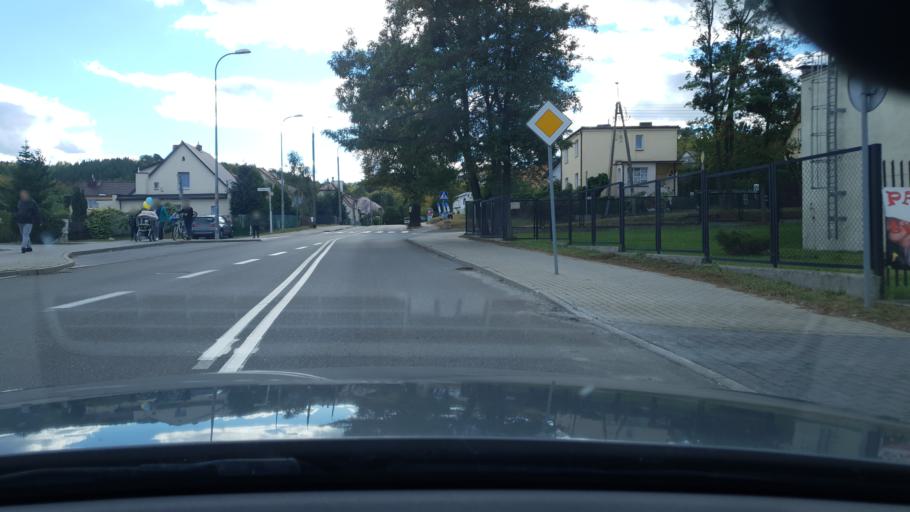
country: PL
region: Pomeranian Voivodeship
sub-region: Powiat wejherowski
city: Reda
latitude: 54.5990
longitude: 18.3469
